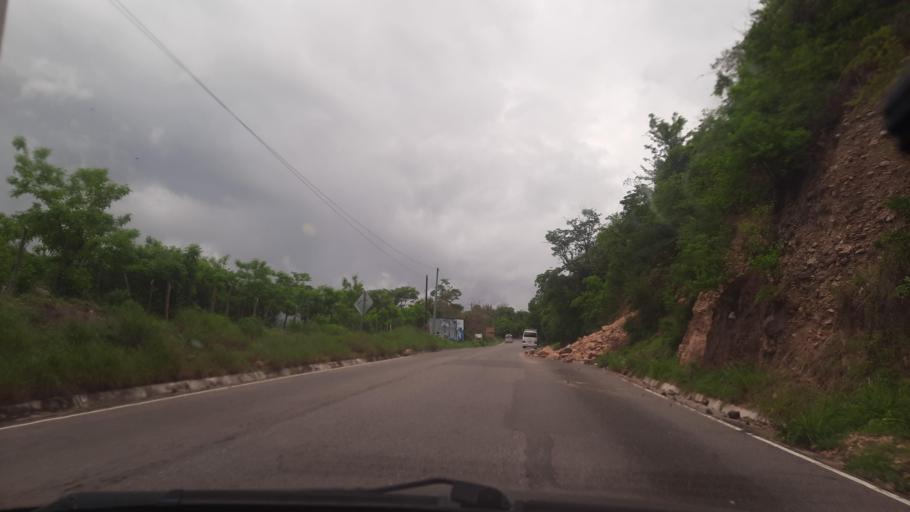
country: GT
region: Chiquimula
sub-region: Municipio de Chiquimula
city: Chiquimula
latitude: 14.8766
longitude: -89.5154
